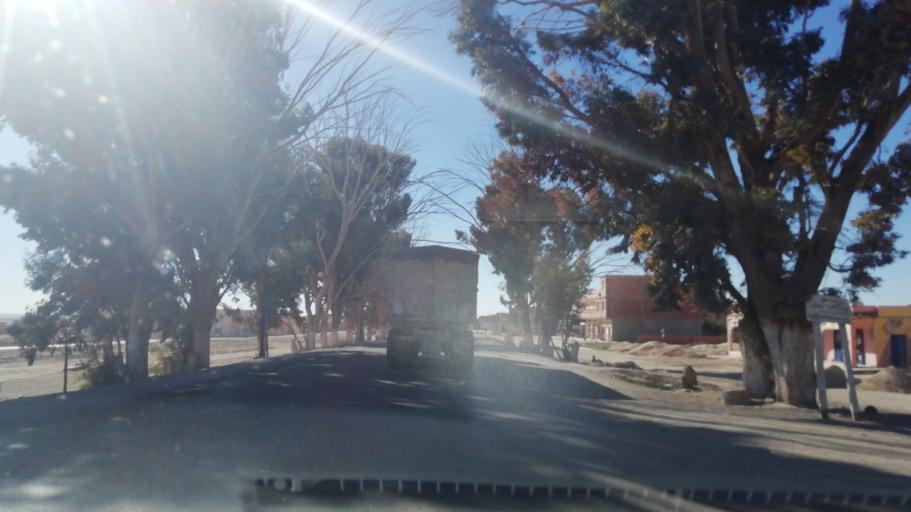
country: DZ
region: Saida
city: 'Ain el Hadjar
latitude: 34.1553
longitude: 0.0704
